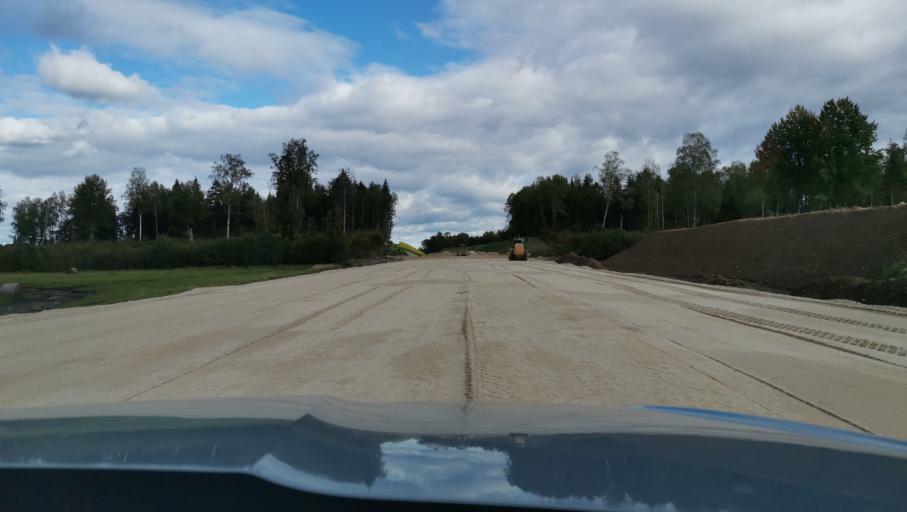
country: EE
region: Harju
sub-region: Keila linn
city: Keila
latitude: 59.1466
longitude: 24.4988
